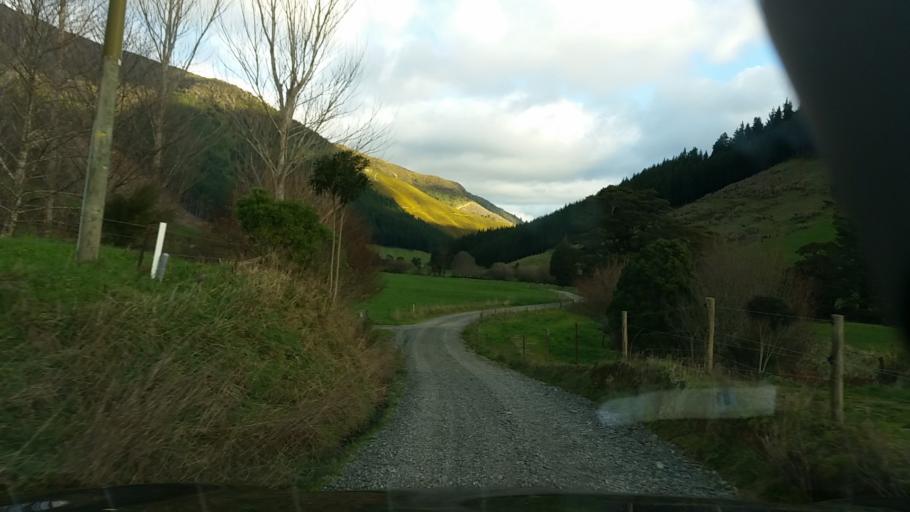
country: NZ
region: Marlborough
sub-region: Marlborough District
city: Picton
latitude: -41.1687
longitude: 173.6506
